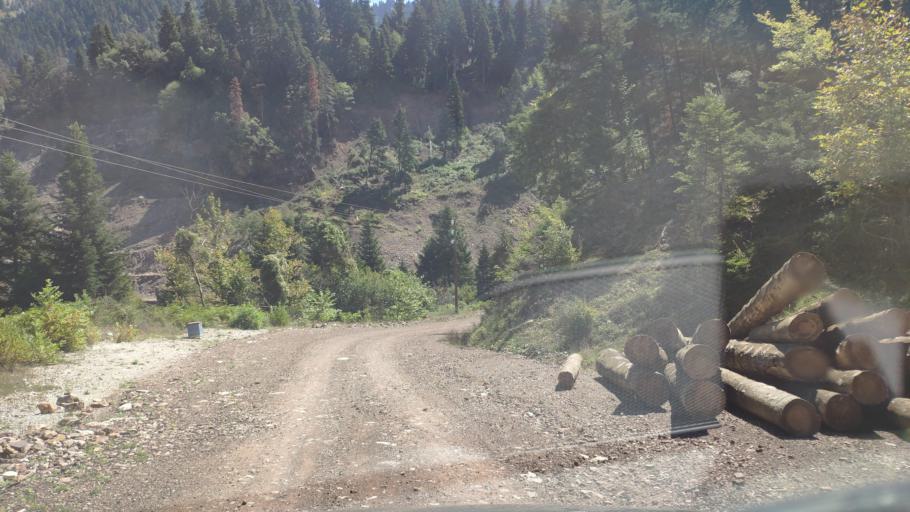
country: GR
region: Central Greece
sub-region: Nomos Evrytanias
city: Kerasochori
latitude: 39.1139
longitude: 21.6215
